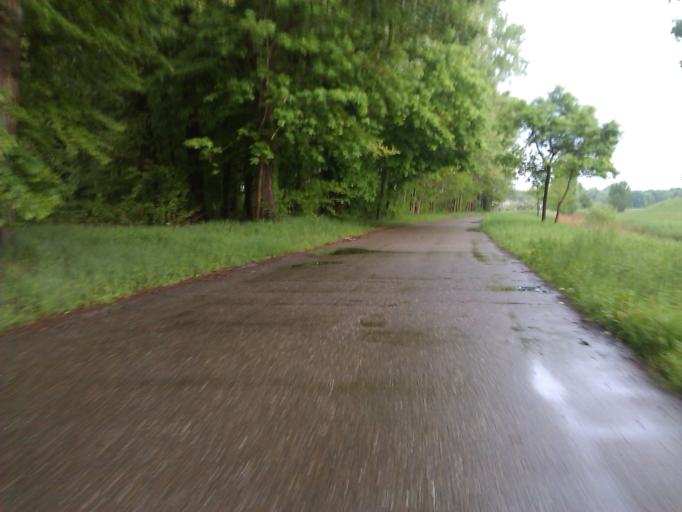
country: DE
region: Baden-Wuerttemberg
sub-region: Karlsruhe Region
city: Lichtenau
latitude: 48.7213
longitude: 7.9684
